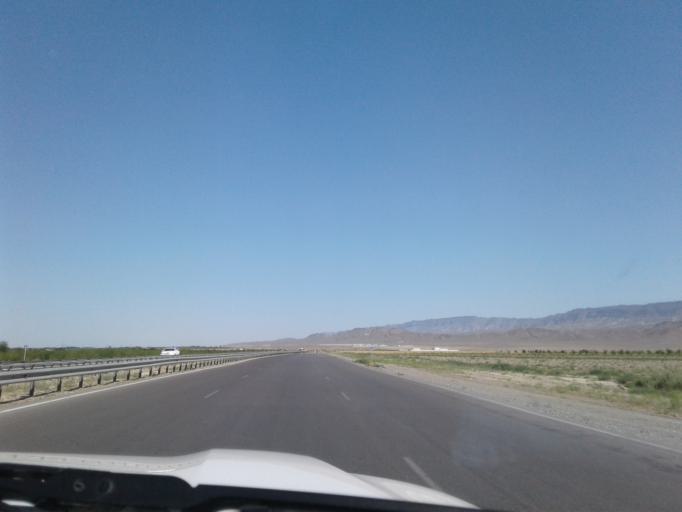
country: TM
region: Ahal
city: Annau
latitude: 37.8179
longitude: 58.7695
